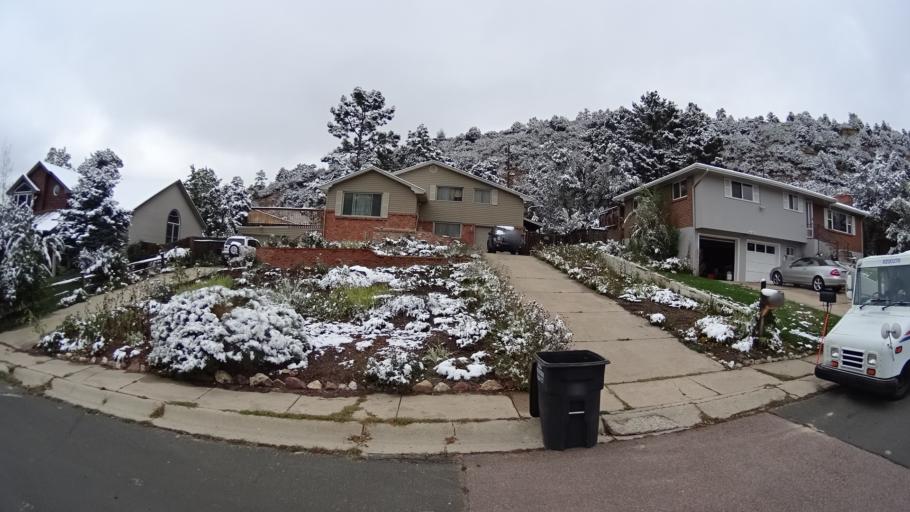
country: US
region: Colorado
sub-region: El Paso County
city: Colorado Springs
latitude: 38.8923
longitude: -104.7817
